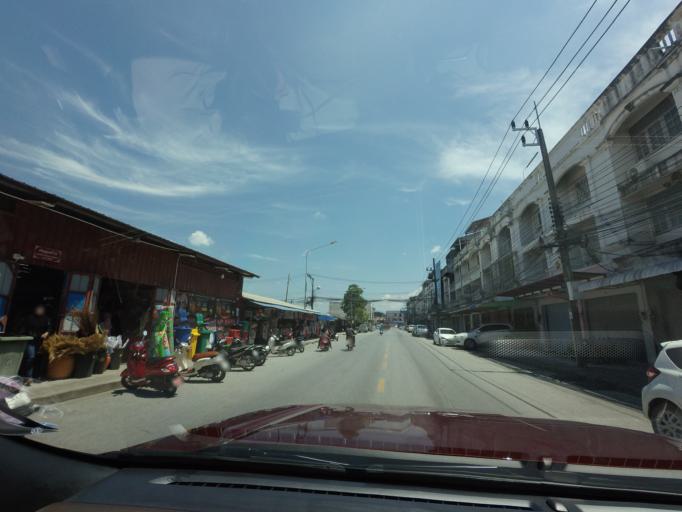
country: TH
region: Yala
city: Yala
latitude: 6.5559
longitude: 101.2815
